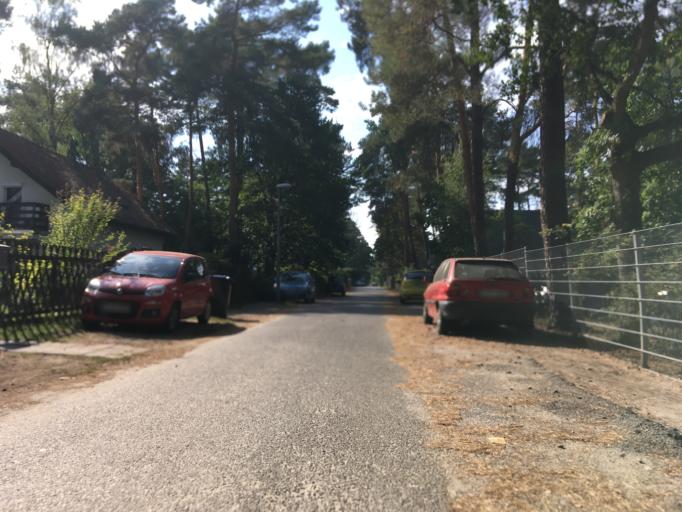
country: DE
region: Berlin
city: Rahnsdorf
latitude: 52.4254
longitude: 13.6770
